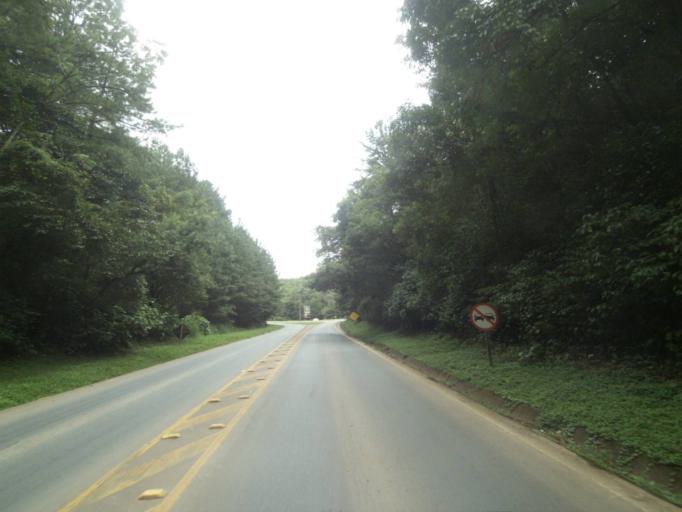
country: BR
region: Parana
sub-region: Telemaco Borba
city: Telemaco Borba
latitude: -24.3107
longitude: -50.6148
